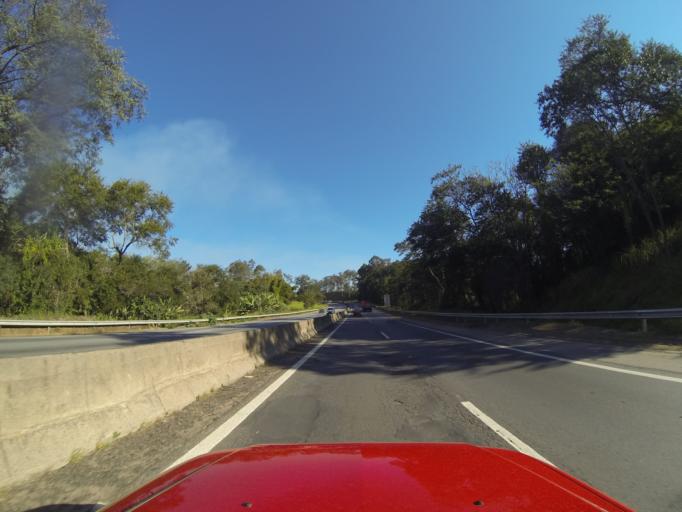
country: BR
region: Sao Paulo
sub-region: Atibaia
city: Atibaia
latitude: -23.0903
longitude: -46.5723
